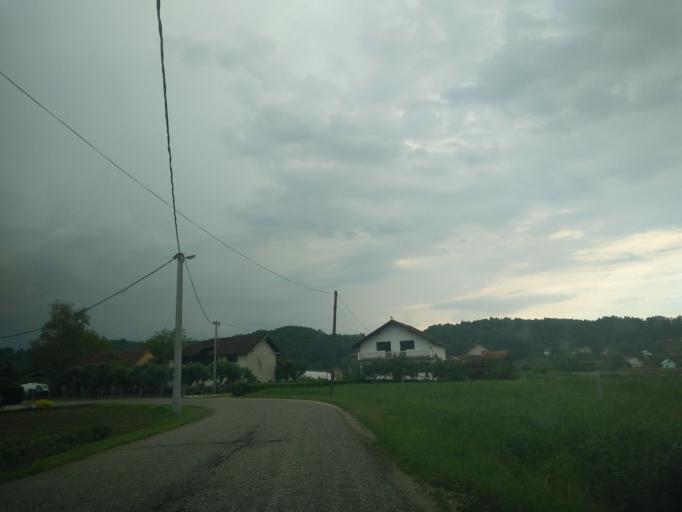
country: BA
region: Republika Srpska
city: Prijedor
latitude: 44.9224
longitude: 16.6969
